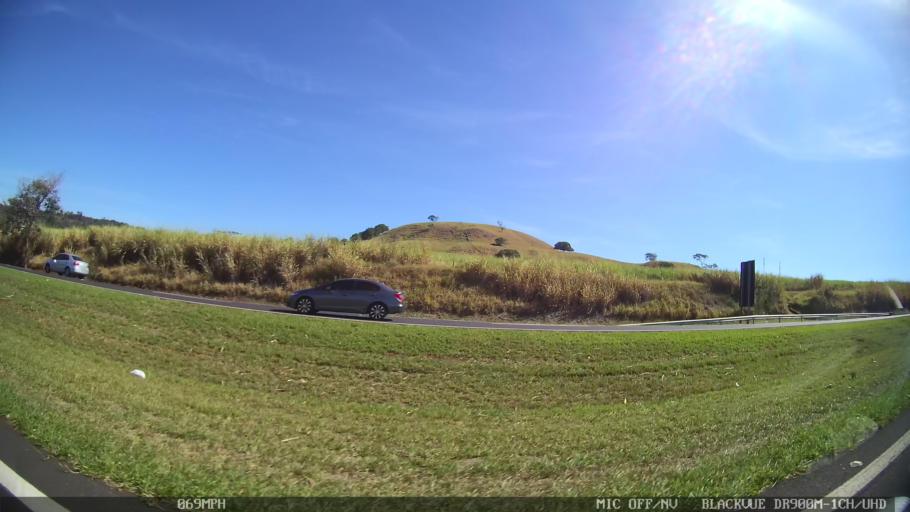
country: BR
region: Sao Paulo
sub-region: Sao Simao
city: Sao Simao
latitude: -21.4786
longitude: -47.6405
